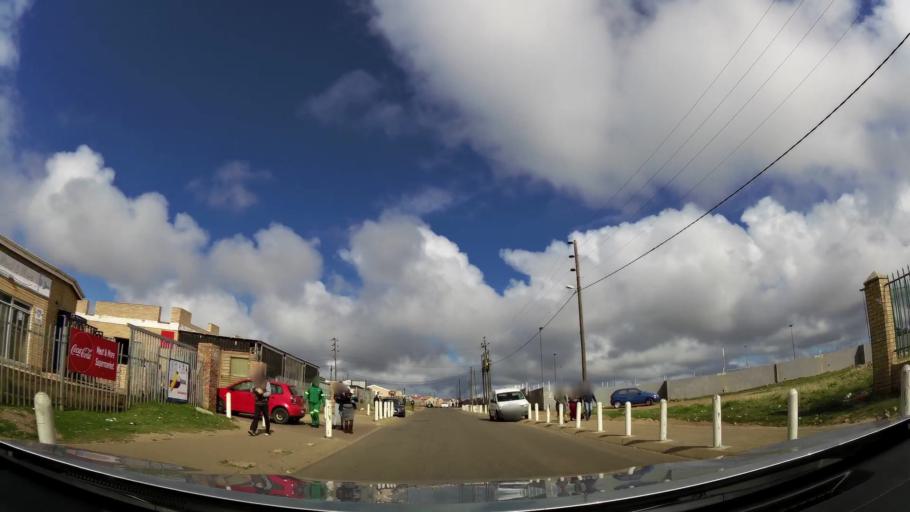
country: ZA
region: Western Cape
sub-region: Eden District Municipality
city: Plettenberg Bay
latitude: -34.0533
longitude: 23.3185
